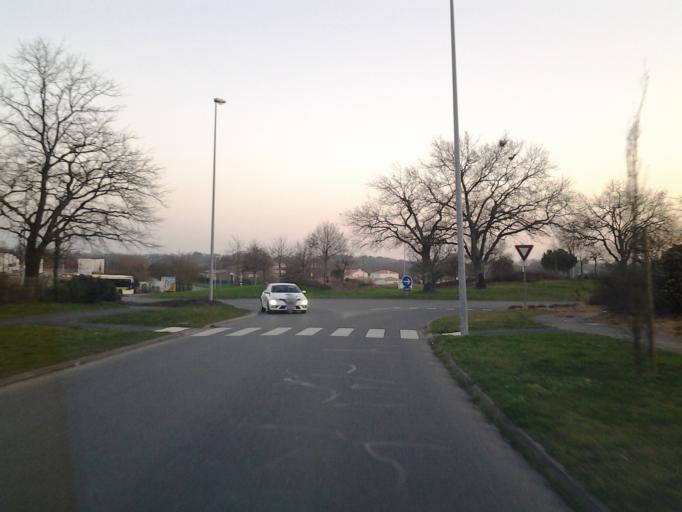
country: FR
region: Pays de la Loire
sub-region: Departement de la Vendee
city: La Roche-sur-Yon
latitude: 46.6550
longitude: -1.4102
